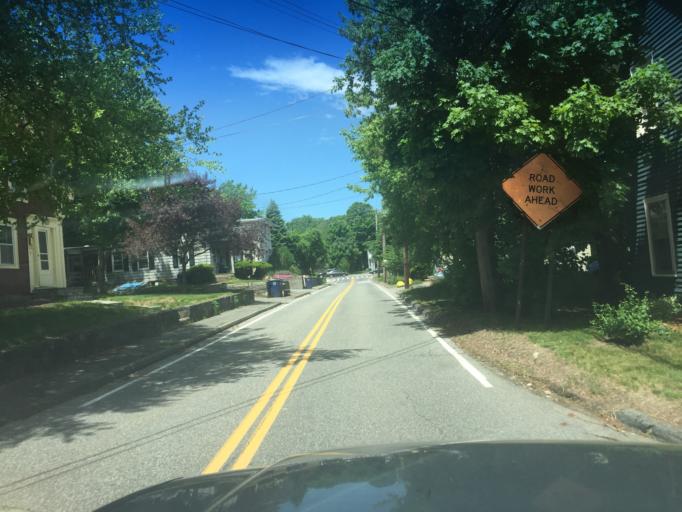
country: US
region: Massachusetts
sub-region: Norfolk County
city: Medway
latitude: 42.1474
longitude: -71.4222
